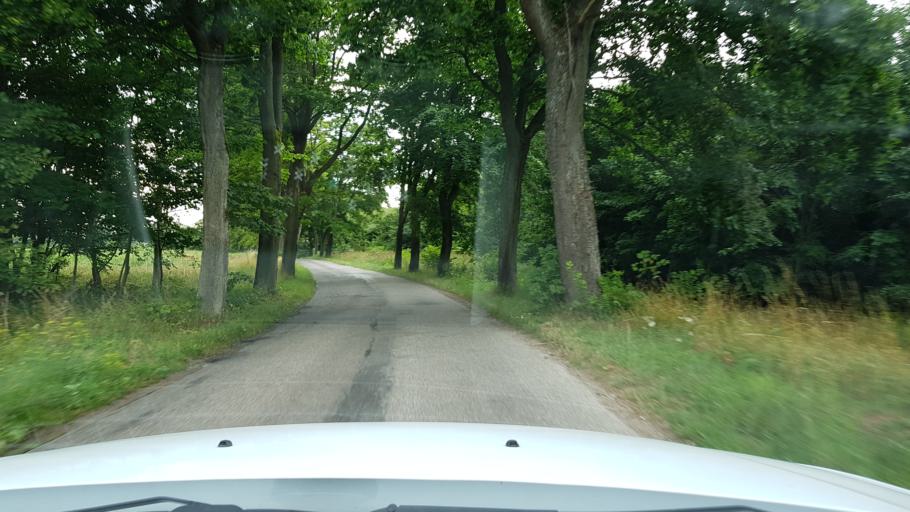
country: PL
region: West Pomeranian Voivodeship
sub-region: Powiat drawski
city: Wierzchowo
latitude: 53.4751
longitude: 16.0664
